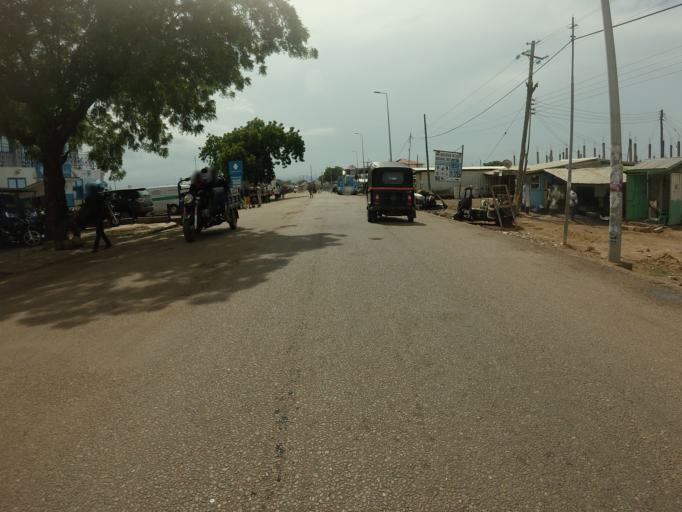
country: GH
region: Upper East
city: Bolgatanga
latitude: 10.7835
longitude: -0.8486
